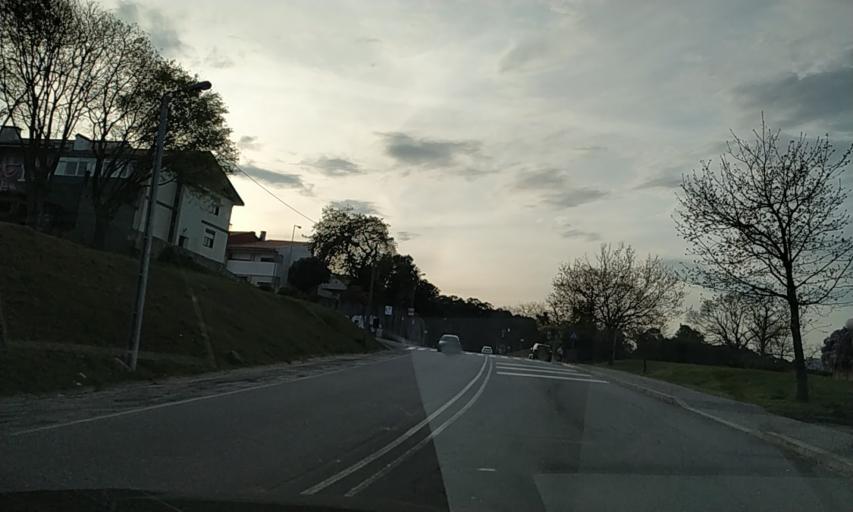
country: PT
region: Porto
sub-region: Maia
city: Leca do Bailio
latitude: 41.2073
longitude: -8.6216
